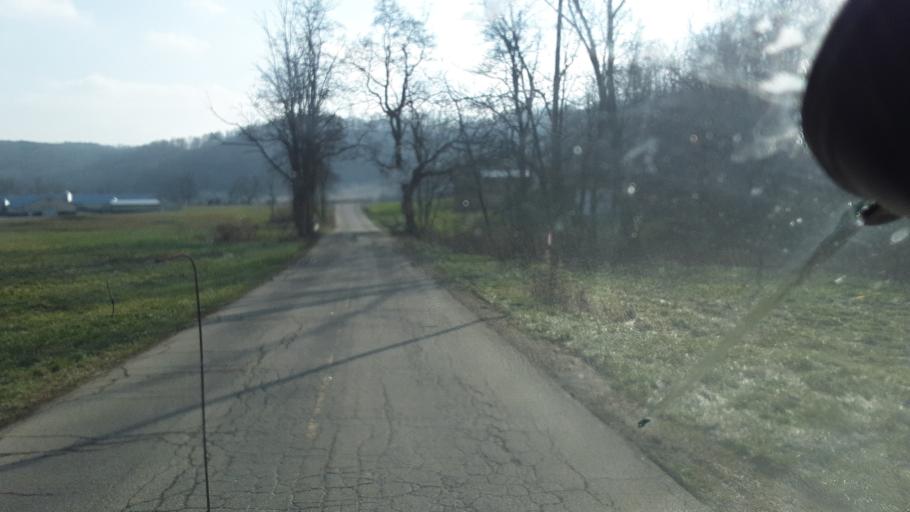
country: US
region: Ohio
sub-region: Knox County
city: Oak Hill
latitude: 40.4329
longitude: -82.2035
